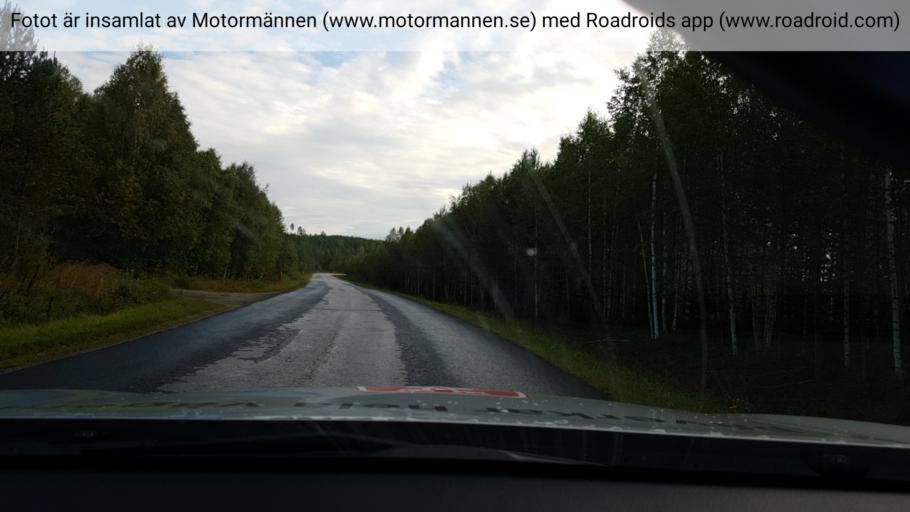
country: SE
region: Vaesterbotten
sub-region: Vindelns Kommun
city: Vindeln
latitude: 64.2030
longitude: 19.7456
